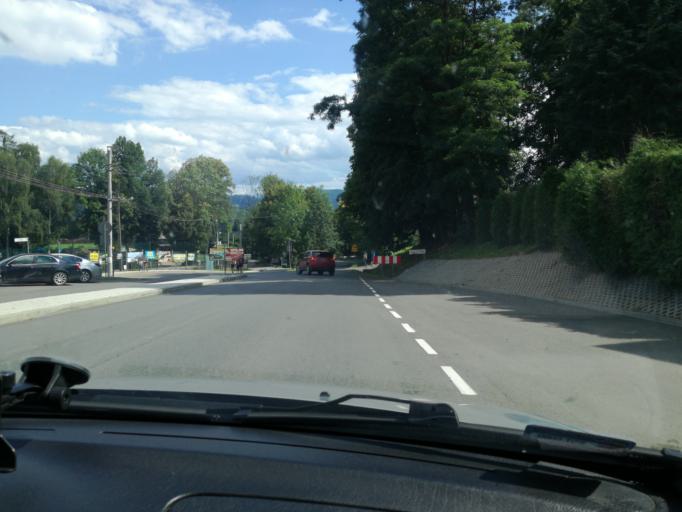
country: PL
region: Subcarpathian Voivodeship
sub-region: Powiat leski
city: Polanczyk
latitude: 49.3638
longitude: 22.4262
